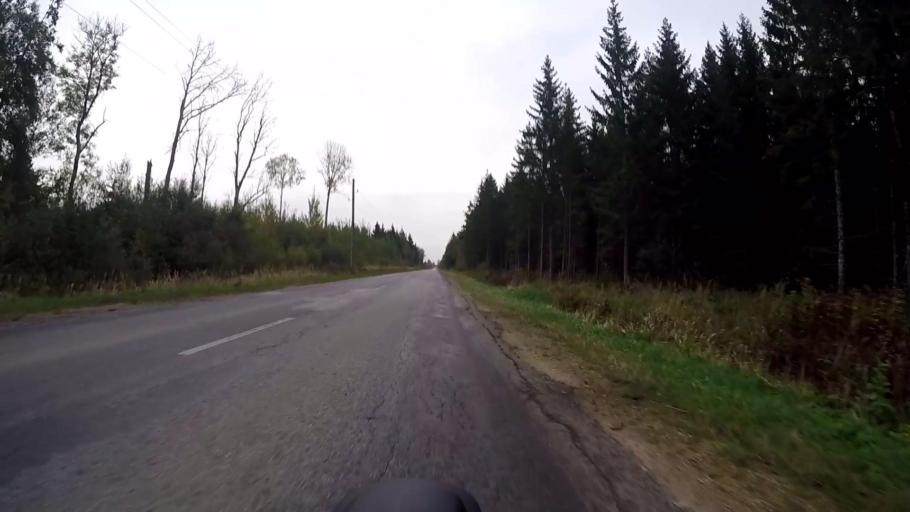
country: LV
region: Saulkrastu
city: Saulkrasti
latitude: 57.2734
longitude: 24.5124
